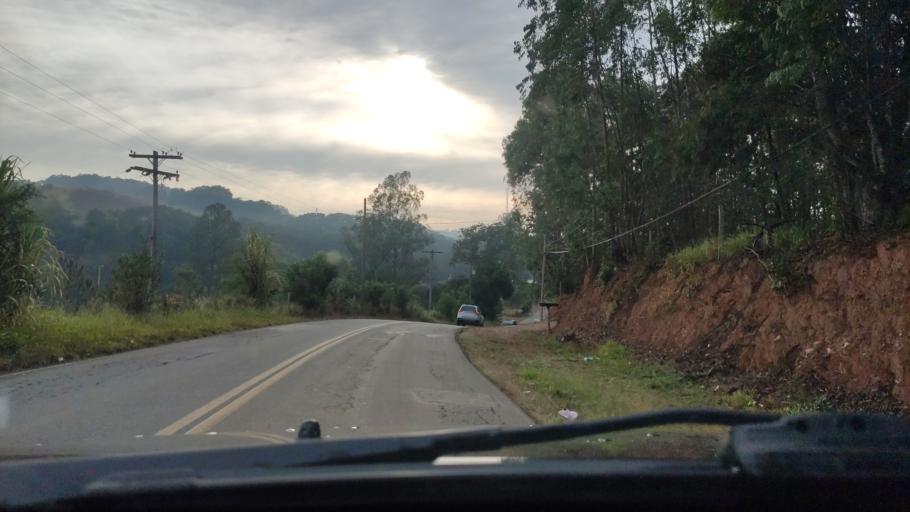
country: BR
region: Sao Paulo
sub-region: Jarinu
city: Jarinu
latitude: -23.1209
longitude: -46.7684
